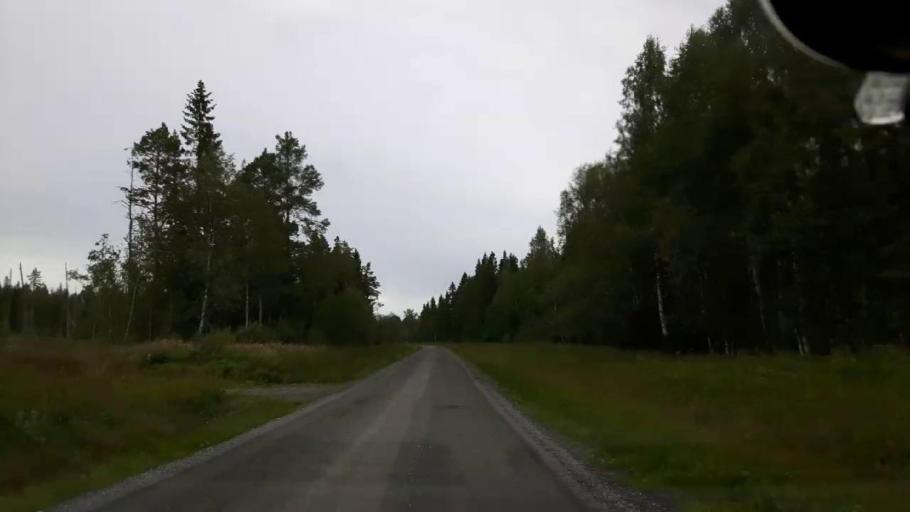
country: SE
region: Jaemtland
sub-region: Krokoms Kommun
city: Krokom
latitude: 63.2853
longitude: 14.3846
